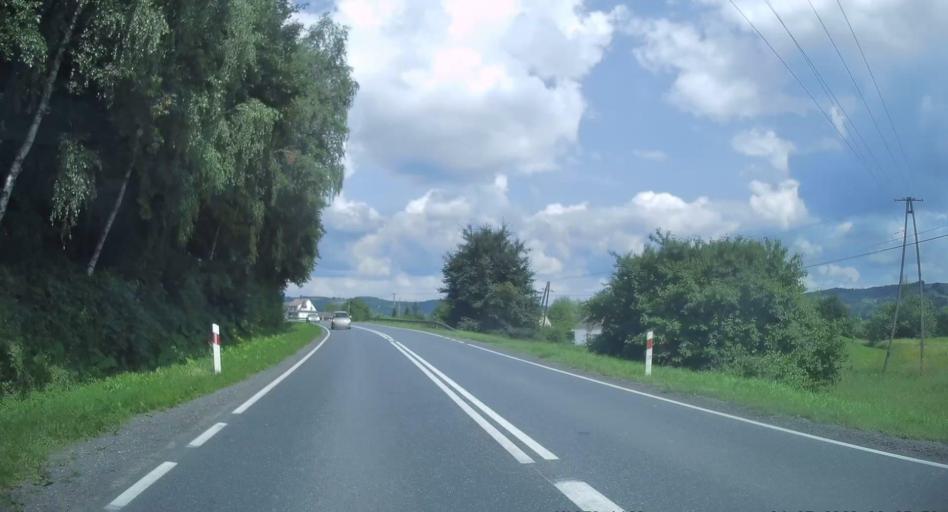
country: PL
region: Lesser Poland Voivodeship
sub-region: Powiat tarnowski
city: Janowice
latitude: 49.8853
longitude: 20.8310
